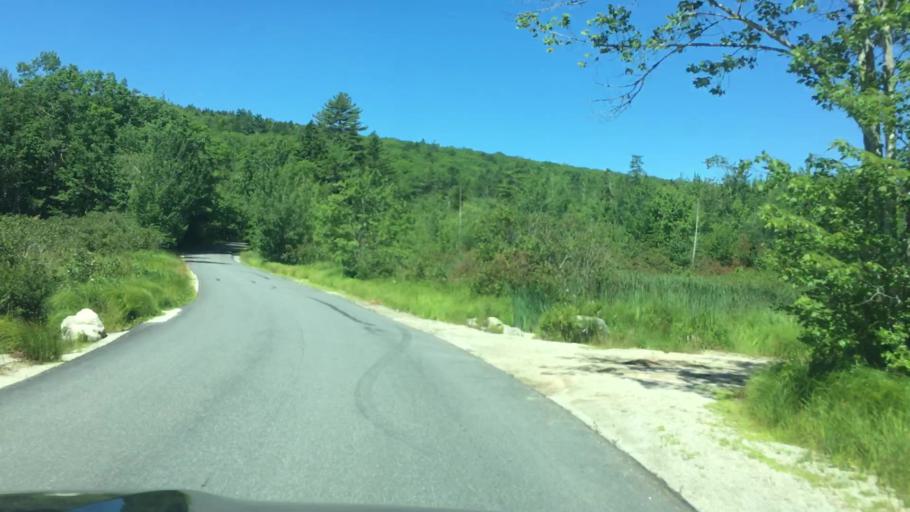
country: US
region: Maine
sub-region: Hancock County
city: Sedgwick
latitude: 44.3322
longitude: -68.6546
